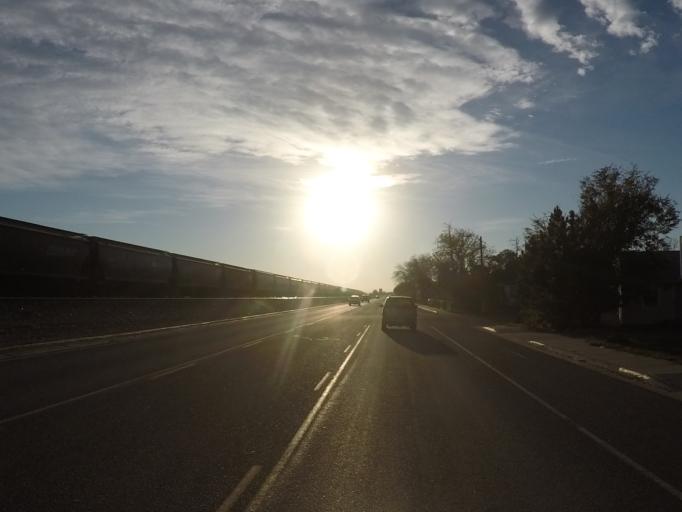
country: US
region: Montana
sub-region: Yellowstone County
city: Laurel
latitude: 45.6739
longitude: -108.7516
